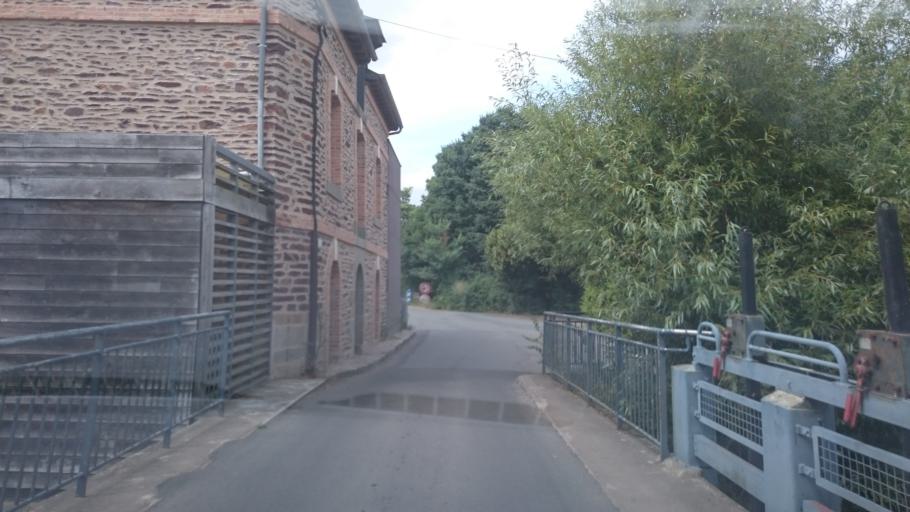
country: FR
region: Brittany
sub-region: Departement d'Ille-et-Vilaine
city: Vezin-le-Coquet
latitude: 48.0945
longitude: -1.7474
